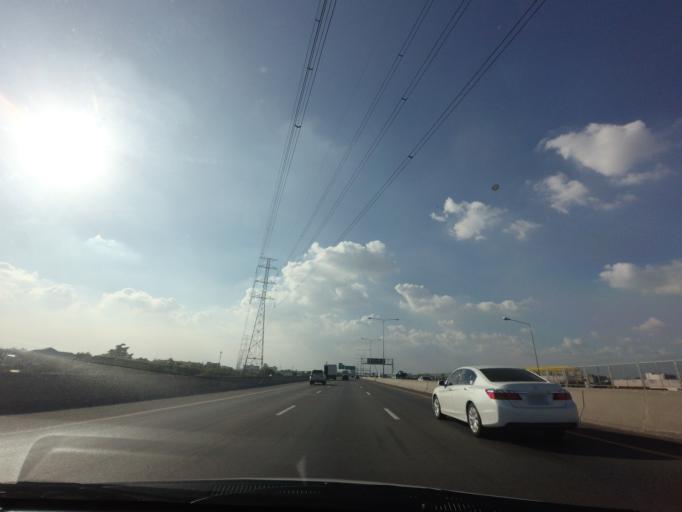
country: TH
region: Samut Prakan
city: Samut Prakan
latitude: 13.6231
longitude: 100.6023
